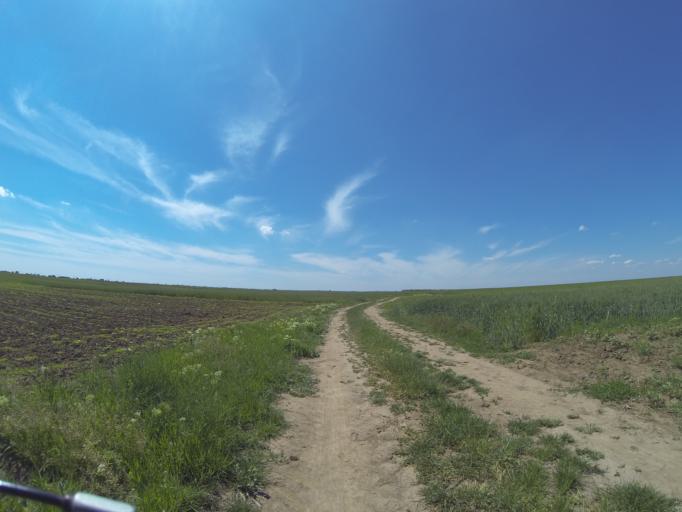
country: RO
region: Dolj
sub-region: Comuna Leu
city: Leu
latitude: 44.2175
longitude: 24.0162
